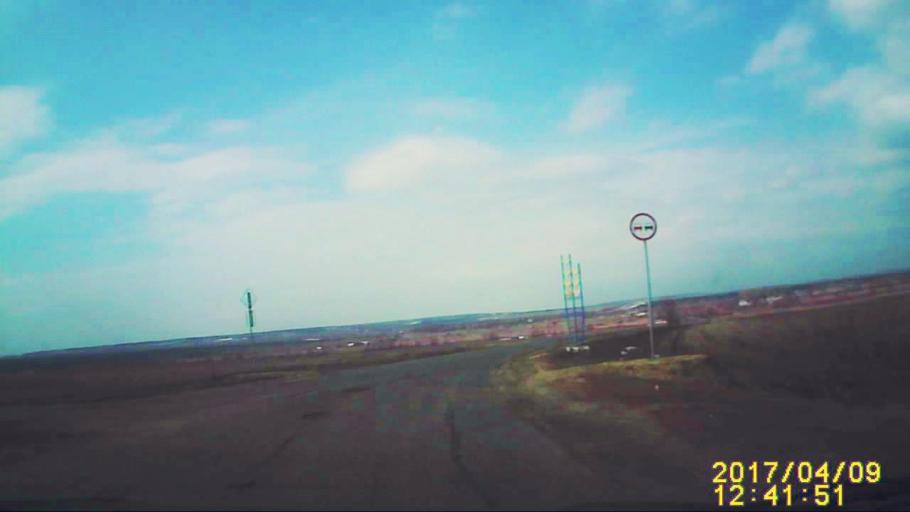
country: RU
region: Ulyanovsk
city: Ignatovka
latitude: 54.0004
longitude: 47.9320
